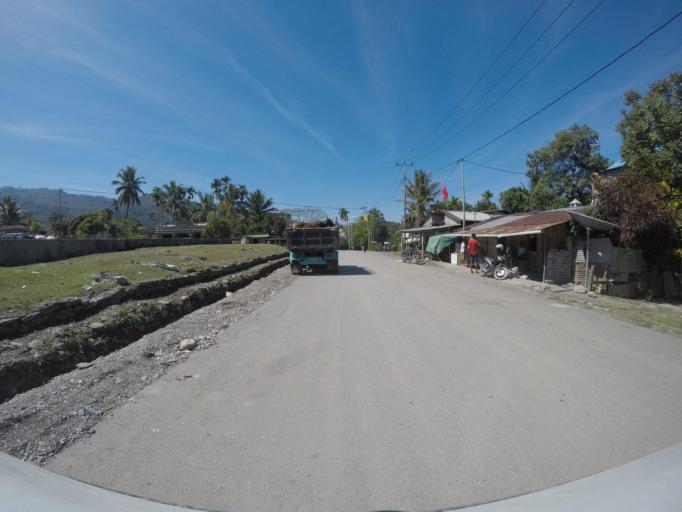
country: TL
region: Ermera
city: Gleno
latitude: -8.8111
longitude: 125.3187
